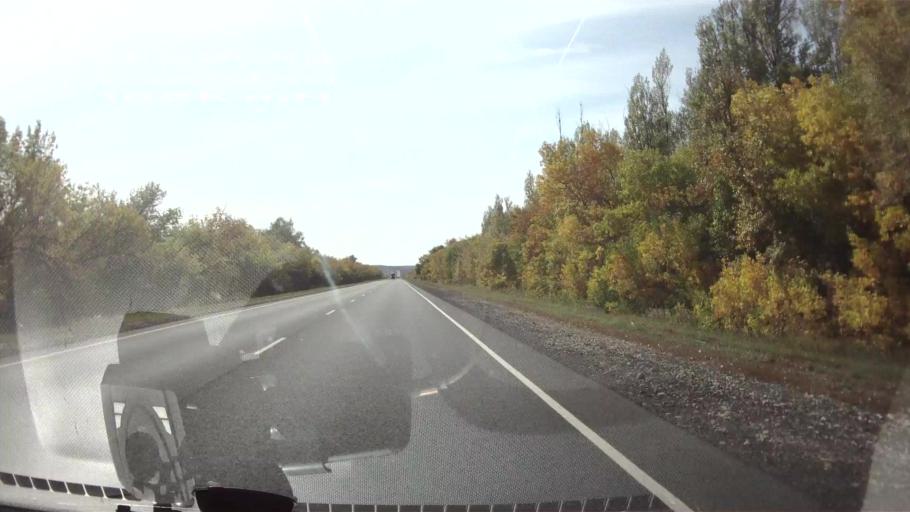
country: RU
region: Saratov
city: Khvalynsk
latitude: 52.5987
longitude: 48.1415
